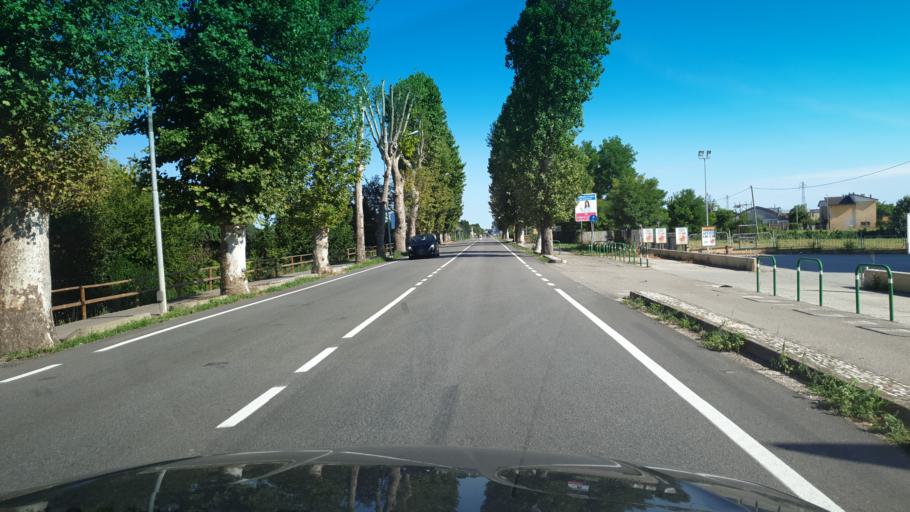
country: IT
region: Veneto
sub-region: Provincia di Padova
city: Stanghella
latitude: 45.1306
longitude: 11.7603
